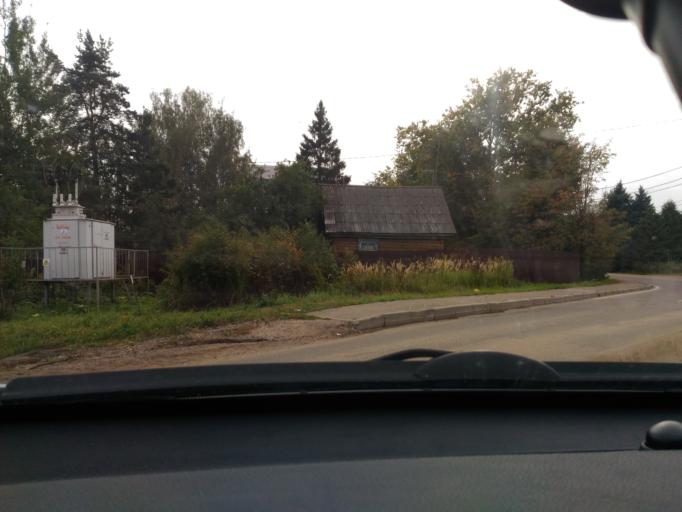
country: RU
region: Moskovskaya
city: Povarovo
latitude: 56.0896
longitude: 37.0613
